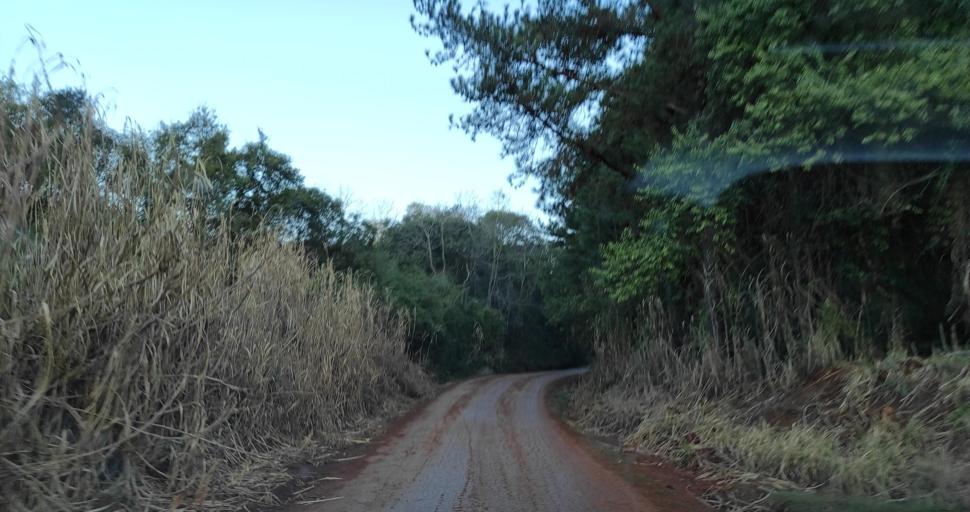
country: AR
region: Misiones
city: Capiovi
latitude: -26.8829
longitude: -55.0857
